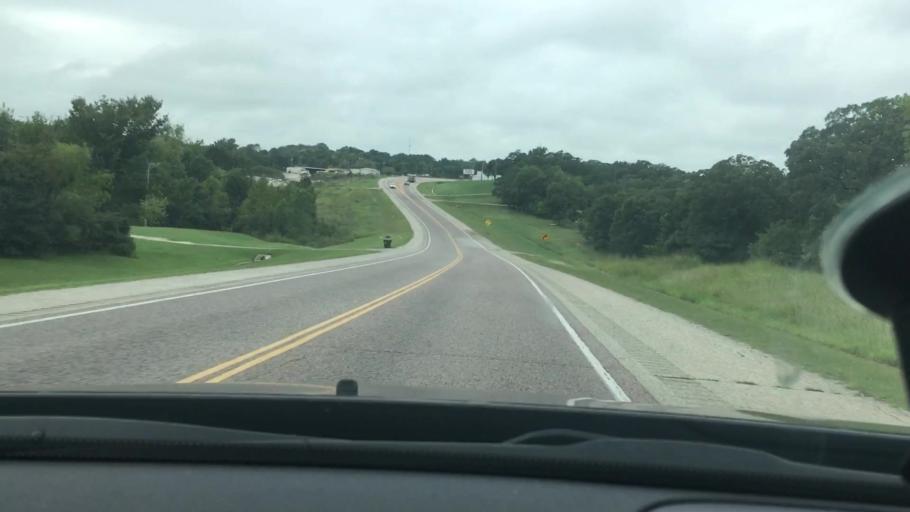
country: US
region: Oklahoma
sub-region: Pontotoc County
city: Ada
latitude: 34.7817
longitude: -96.5794
